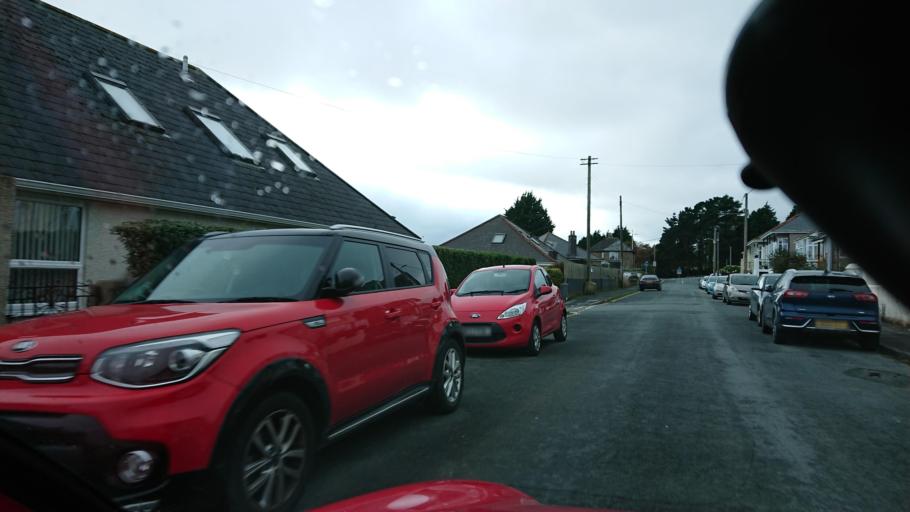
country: GB
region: England
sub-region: Plymouth
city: Plymouth
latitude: 50.4117
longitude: -4.1264
